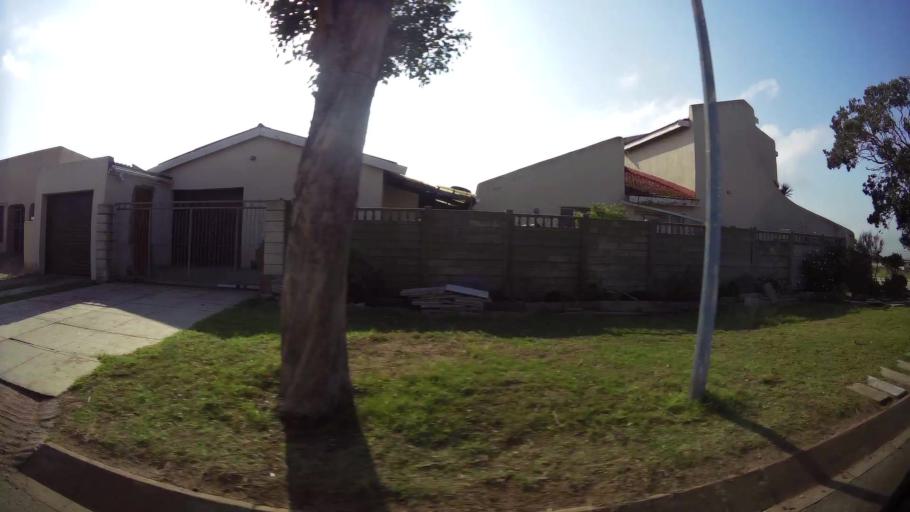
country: ZA
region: Eastern Cape
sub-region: Nelson Mandela Bay Metropolitan Municipality
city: Port Elizabeth
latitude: -33.9239
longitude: 25.5256
